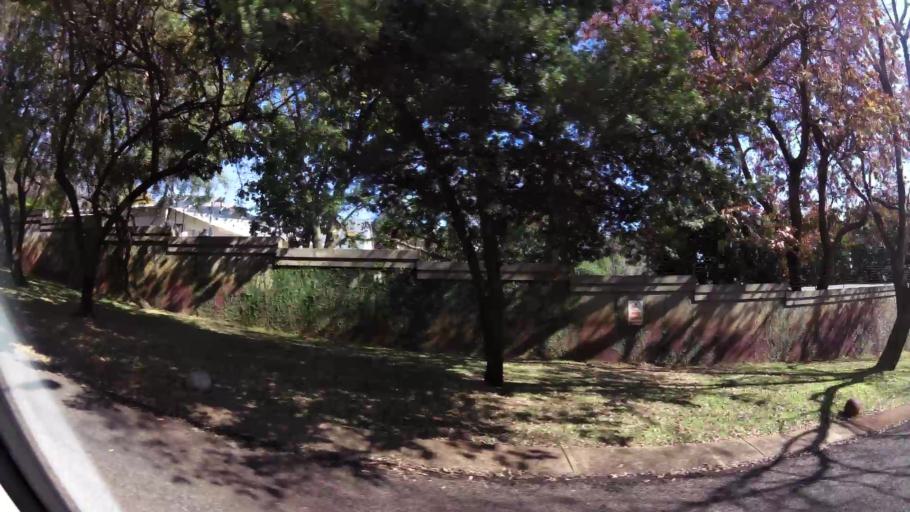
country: ZA
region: Gauteng
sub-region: City of Tshwane Metropolitan Municipality
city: Pretoria
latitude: -25.7799
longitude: 28.2348
